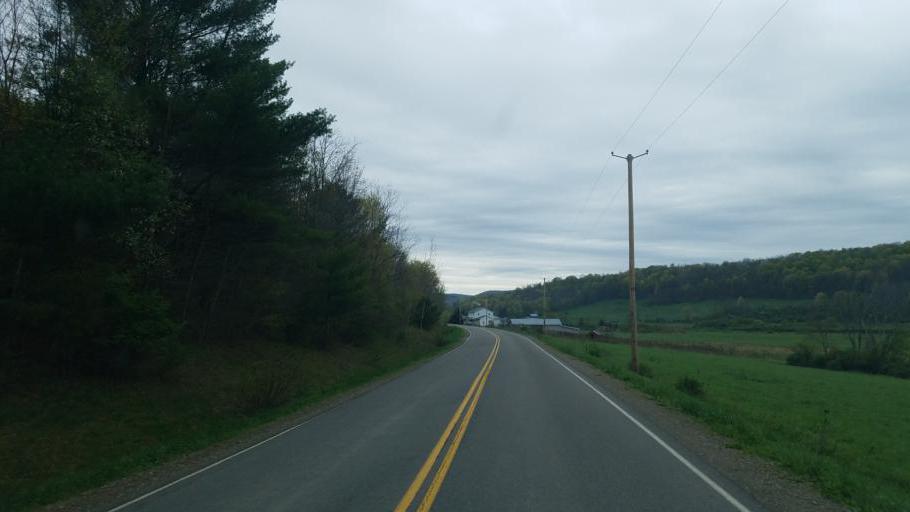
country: US
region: Pennsylvania
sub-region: Tioga County
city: Westfield
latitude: 42.0140
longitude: -77.4737
